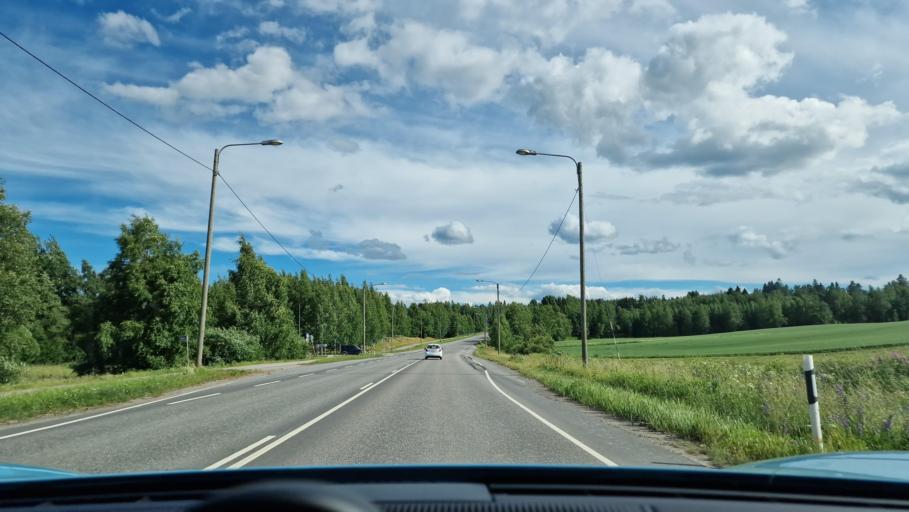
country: FI
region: Pirkanmaa
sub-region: Tampere
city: Orivesi
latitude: 61.6697
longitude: 24.3542
